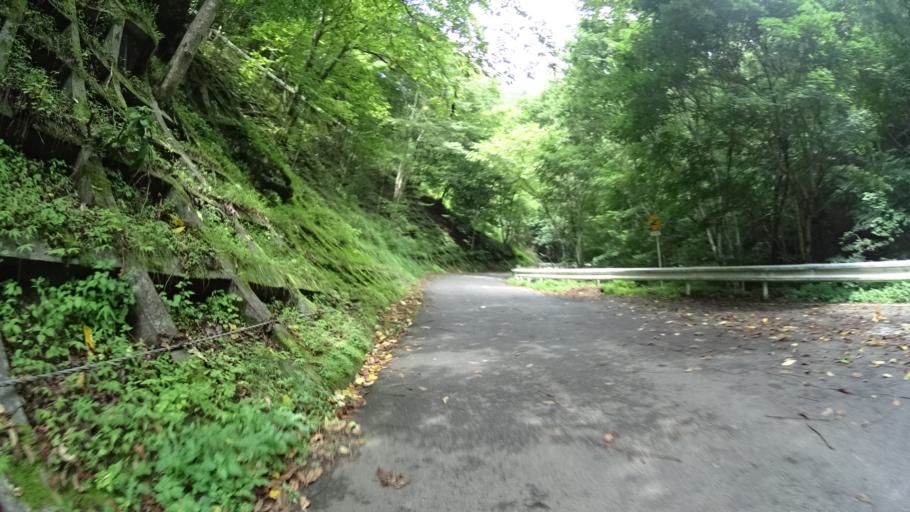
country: JP
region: Nagano
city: Saku
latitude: 36.0655
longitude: 138.6800
